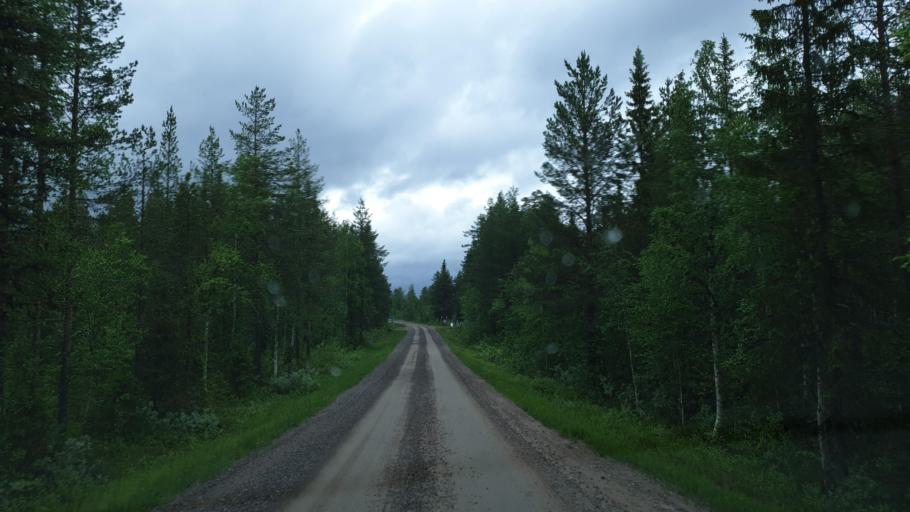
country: SE
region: Norrbotten
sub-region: Arvidsjaurs Kommun
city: Arvidsjaur
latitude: 65.6074
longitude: 19.0927
